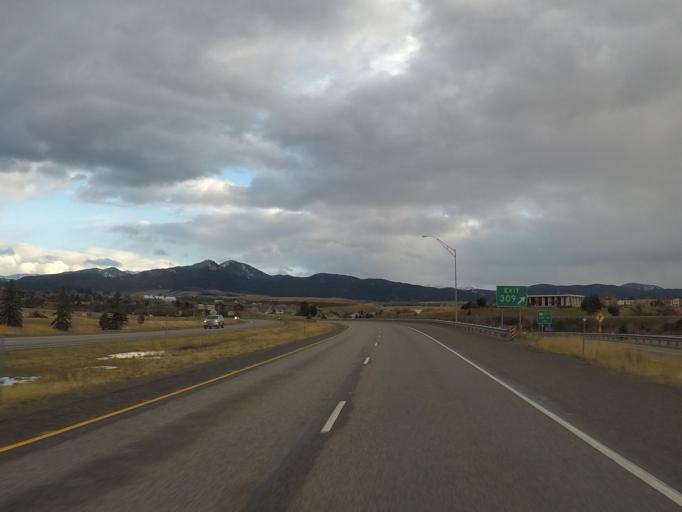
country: US
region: Montana
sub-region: Gallatin County
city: Bozeman
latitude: 45.6781
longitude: -111.0120
